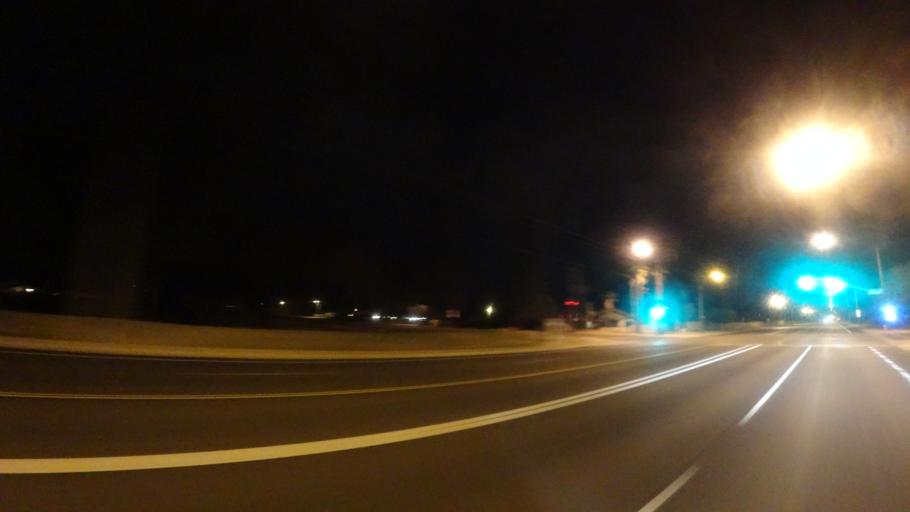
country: US
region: Arizona
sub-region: Maricopa County
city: Mesa
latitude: 33.4451
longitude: -111.7017
